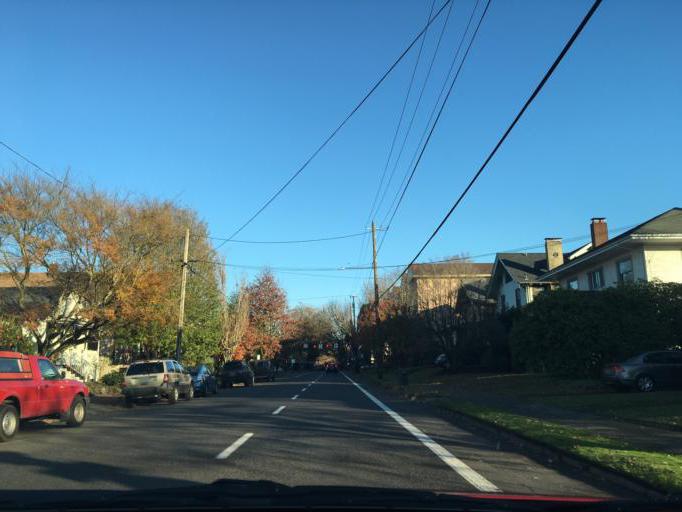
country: US
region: Oregon
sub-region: Multnomah County
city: Portland
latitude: 45.5343
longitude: -122.6466
